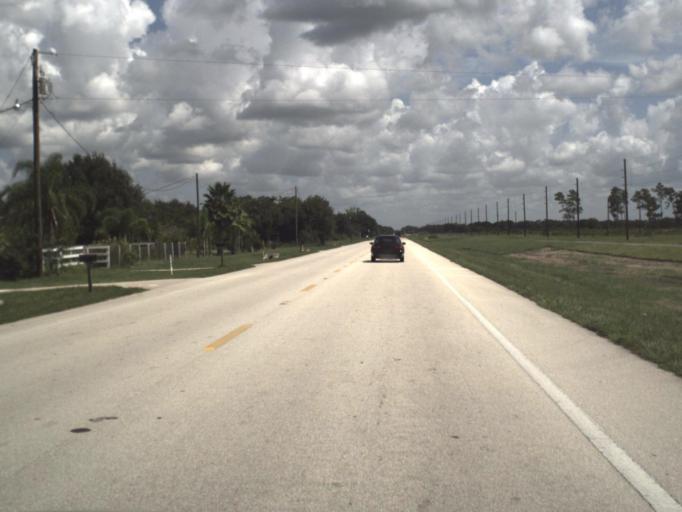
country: US
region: Florida
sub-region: DeSoto County
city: Nocatee
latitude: 27.1379
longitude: -81.8989
